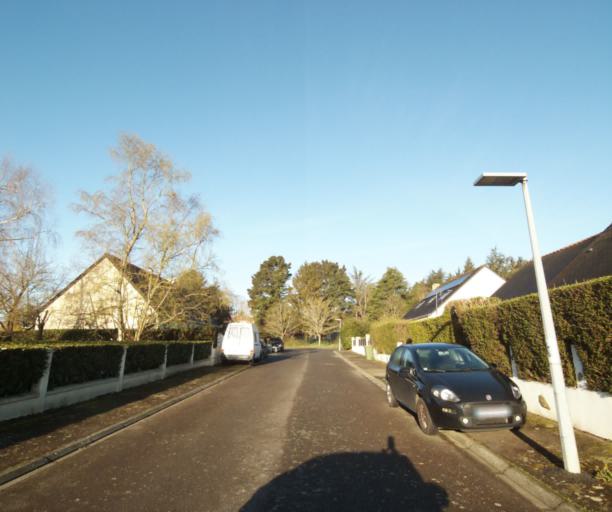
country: FR
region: Pays de la Loire
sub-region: Departement de la Loire-Atlantique
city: Bouvron
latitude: 47.4145
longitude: -1.8424
